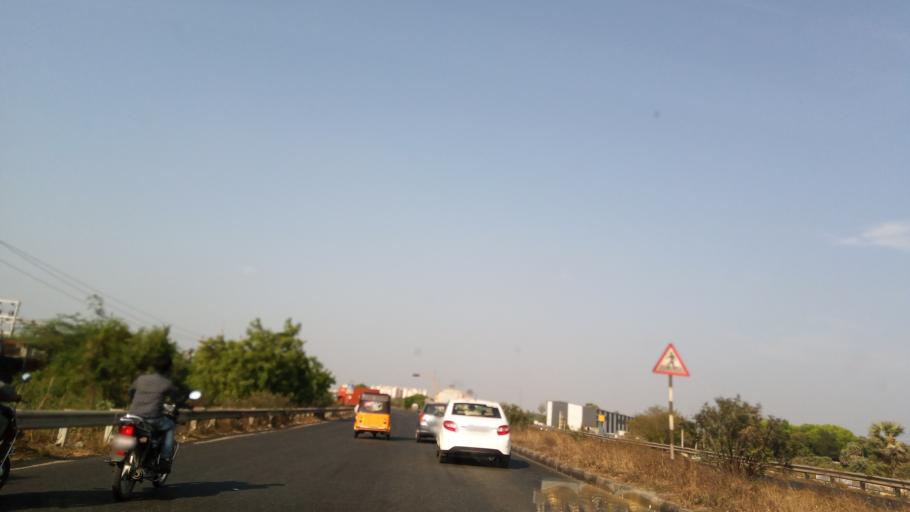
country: IN
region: Tamil Nadu
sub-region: Kancheepuram
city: Nandambakkam
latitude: 13.0178
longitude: 80.0095
